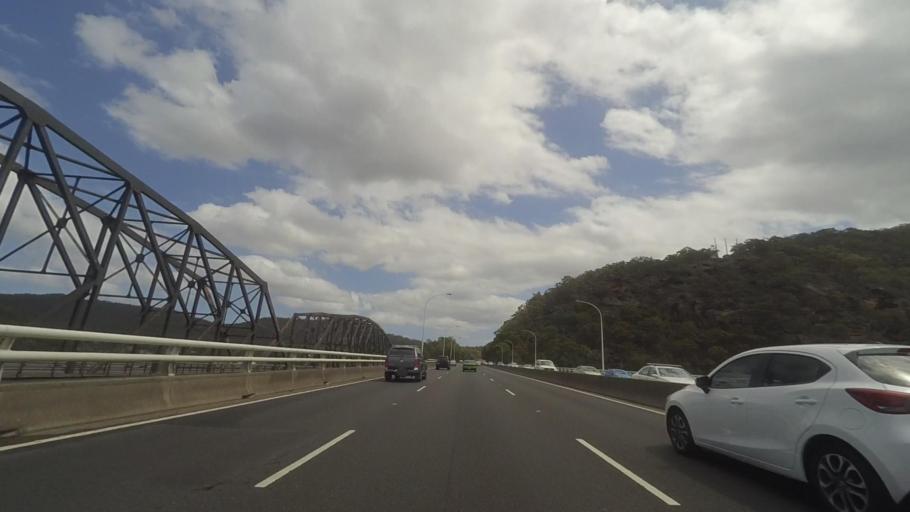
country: AU
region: New South Wales
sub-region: Hornsby Shire
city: Berowra
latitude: -33.5386
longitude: 151.1989
